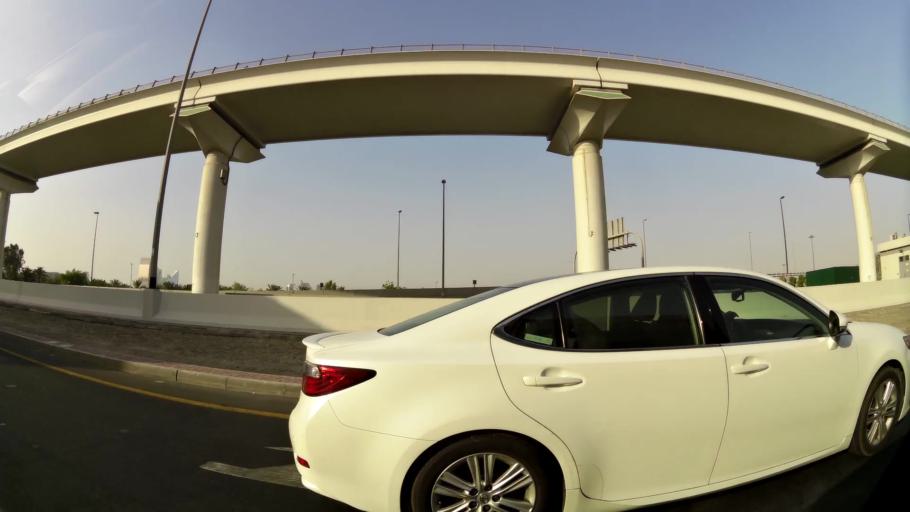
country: AE
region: Ash Shariqah
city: Sharjah
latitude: 25.2495
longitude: 55.3128
